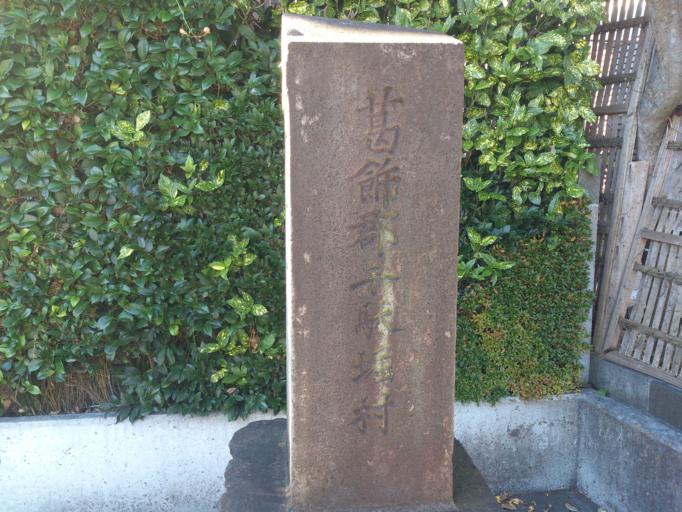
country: JP
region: Chiba
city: Matsudo
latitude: 35.7904
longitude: 139.9327
